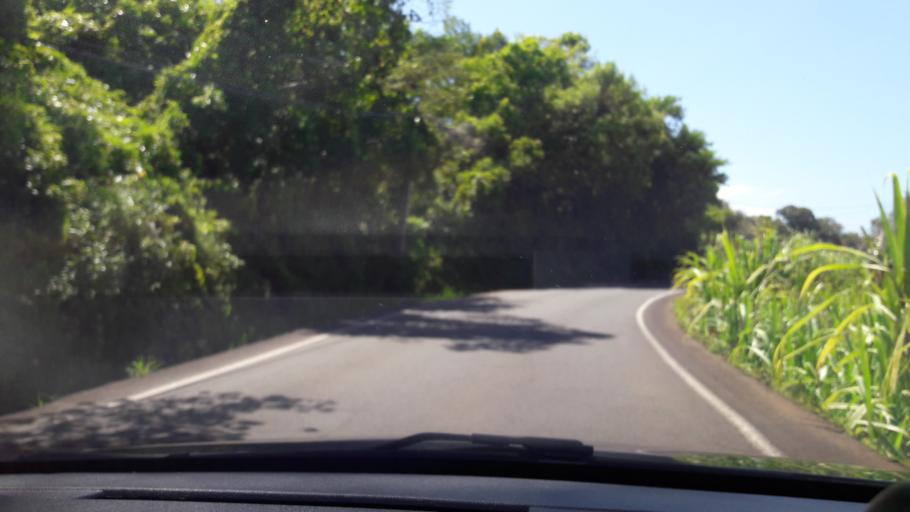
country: RE
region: Reunion
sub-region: Reunion
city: Saint-Benoit
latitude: -21.0919
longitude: 55.7033
